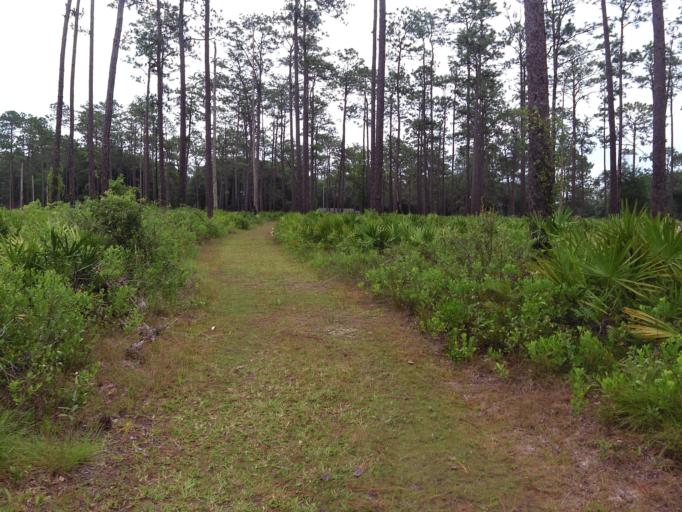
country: US
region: Florida
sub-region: Union County
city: Lake Butler
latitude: 30.2147
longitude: -82.3905
